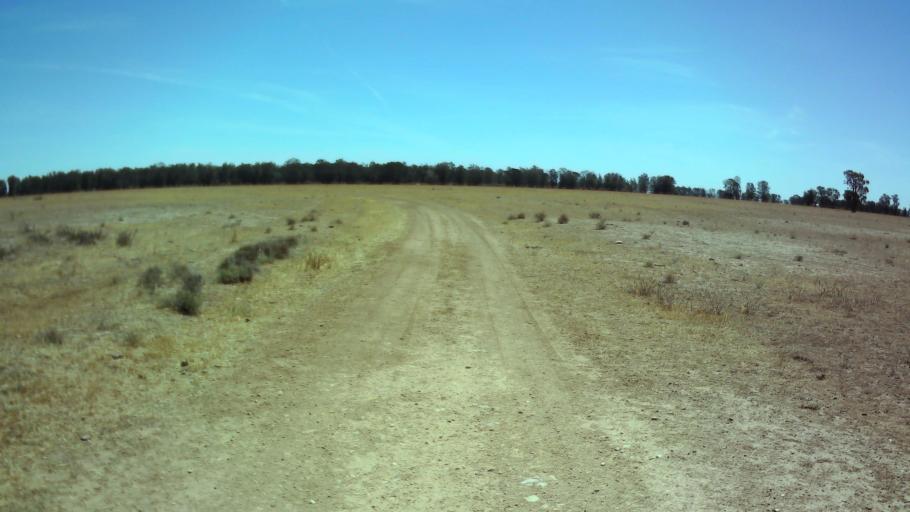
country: AU
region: New South Wales
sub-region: Bland
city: West Wyalong
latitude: -33.8388
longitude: 147.6310
